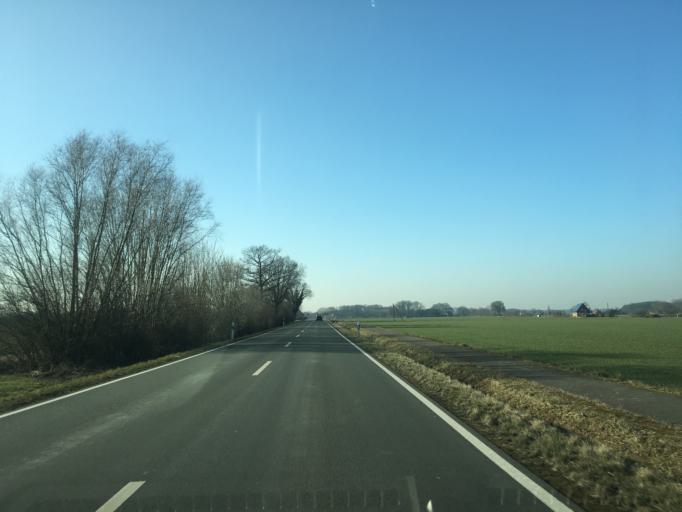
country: DE
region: North Rhine-Westphalia
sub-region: Regierungsbezirk Munster
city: Havixbeck
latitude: 52.0080
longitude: 7.3818
